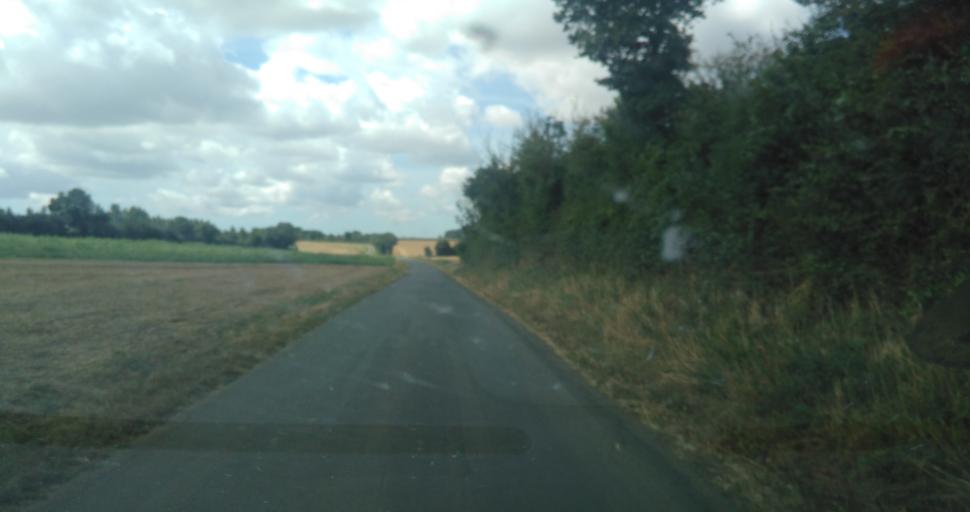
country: FR
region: Pays de la Loire
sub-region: Departement de la Vendee
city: Sainte-Hermine
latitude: 46.5301
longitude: -1.0894
